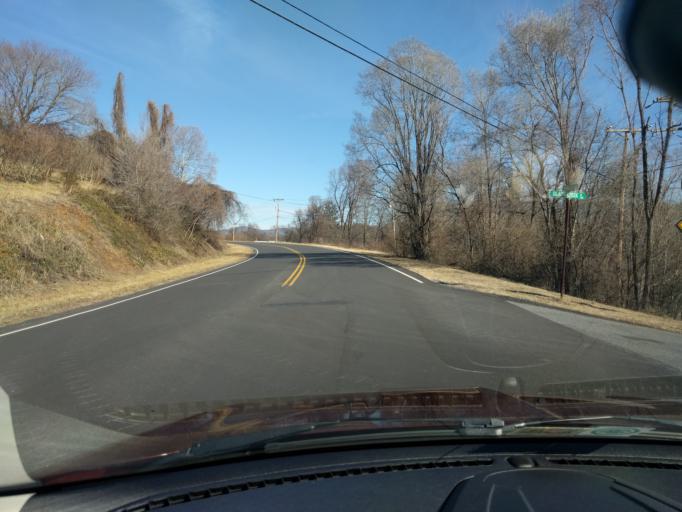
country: US
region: Virginia
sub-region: Botetourt County
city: Laymantown
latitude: 37.3236
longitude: -79.8685
